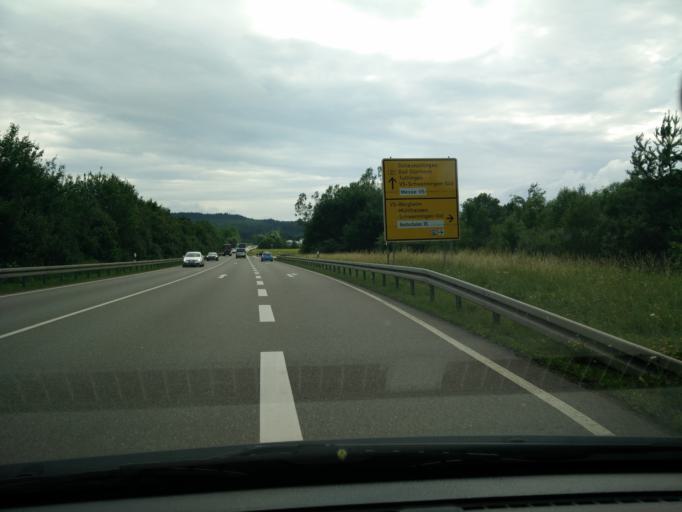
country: DE
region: Baden-Wuerttemberg
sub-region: Freiburg Region
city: Dauchingen
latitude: 48.0628
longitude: 8.5751
